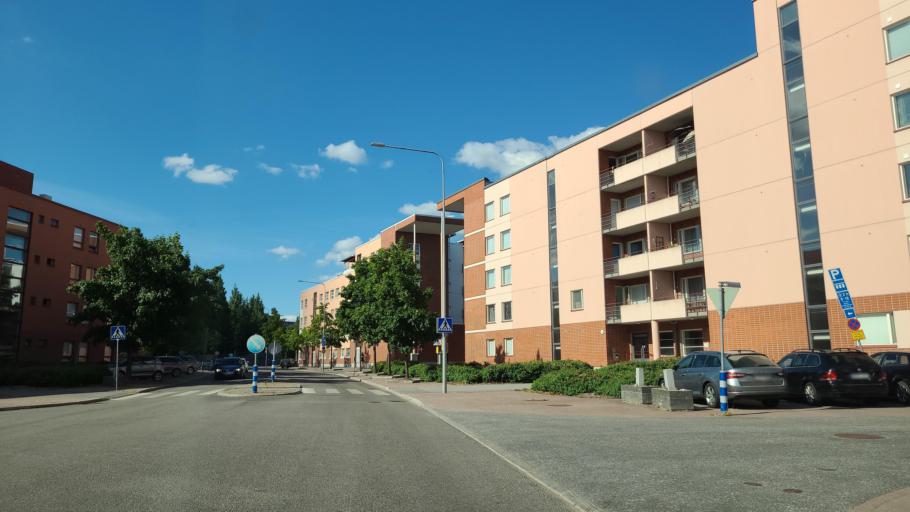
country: FI
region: Central Finland
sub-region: Jyvaeskylae
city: Jyvaeskylae
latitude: 62.2417
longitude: 25.7620
